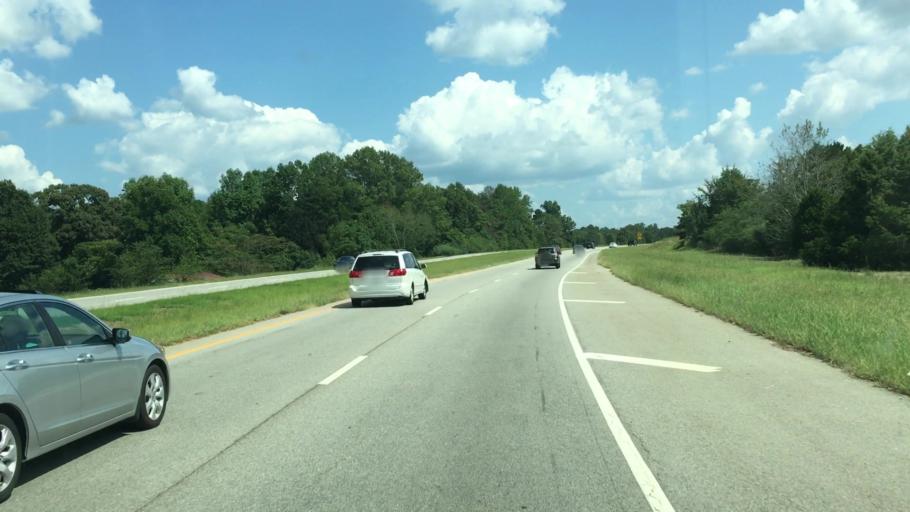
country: US
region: Georgia
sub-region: Putnam County
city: Eatonton
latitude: 33.2954
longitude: -83.3799
